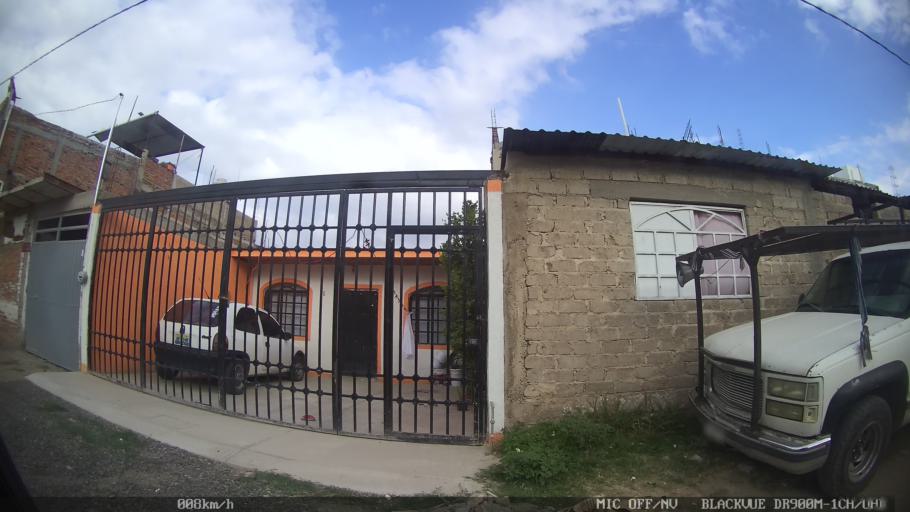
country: MX
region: Jalisco
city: Tonala
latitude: 20.6673
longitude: -103.2380
